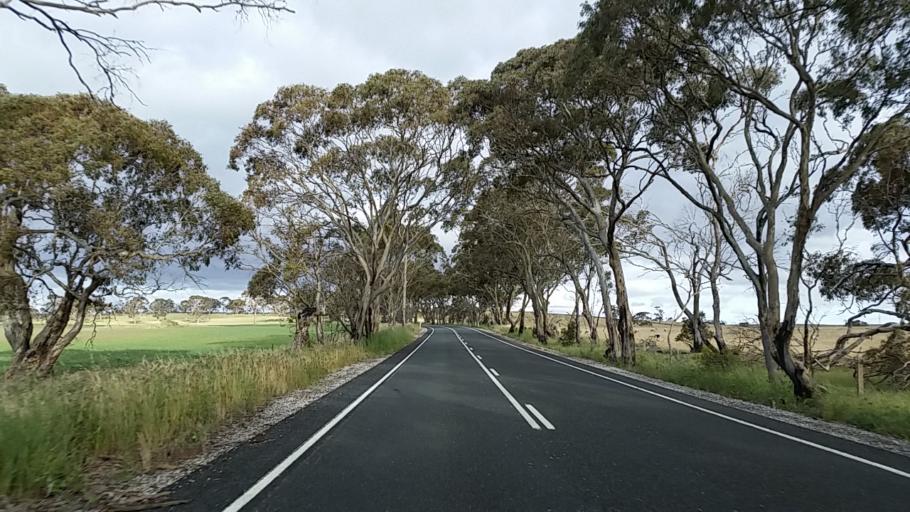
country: AU
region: South Australia
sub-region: Barossa
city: Angaston
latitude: -34.5639
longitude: 139.1791
